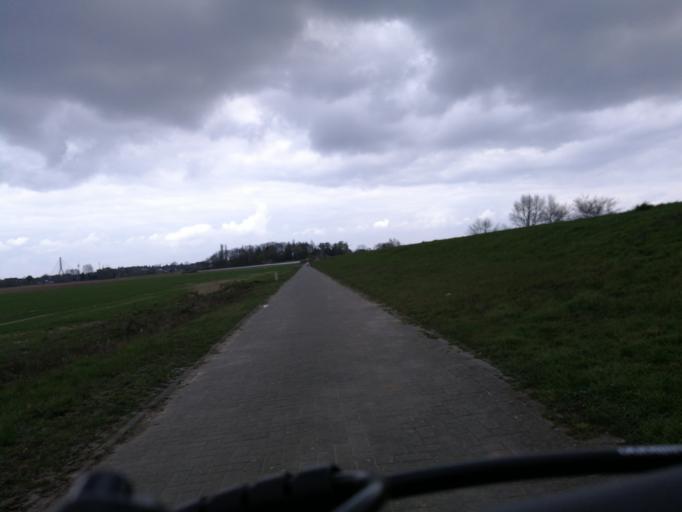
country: DE
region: North Rhine-Westphalia
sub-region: Regierungsbezirk Dusseldorf
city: Dusseldorf
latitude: 51.1533
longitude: 6.7891
